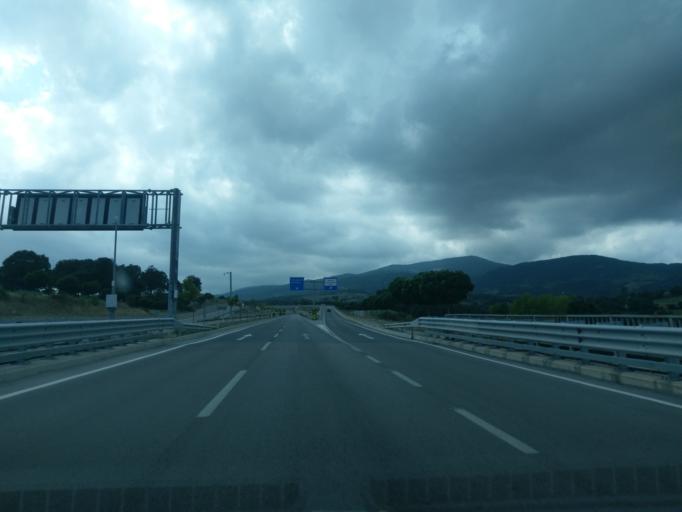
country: TR
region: Sinop
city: Gerze
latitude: 41.8163
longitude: 35.1674
